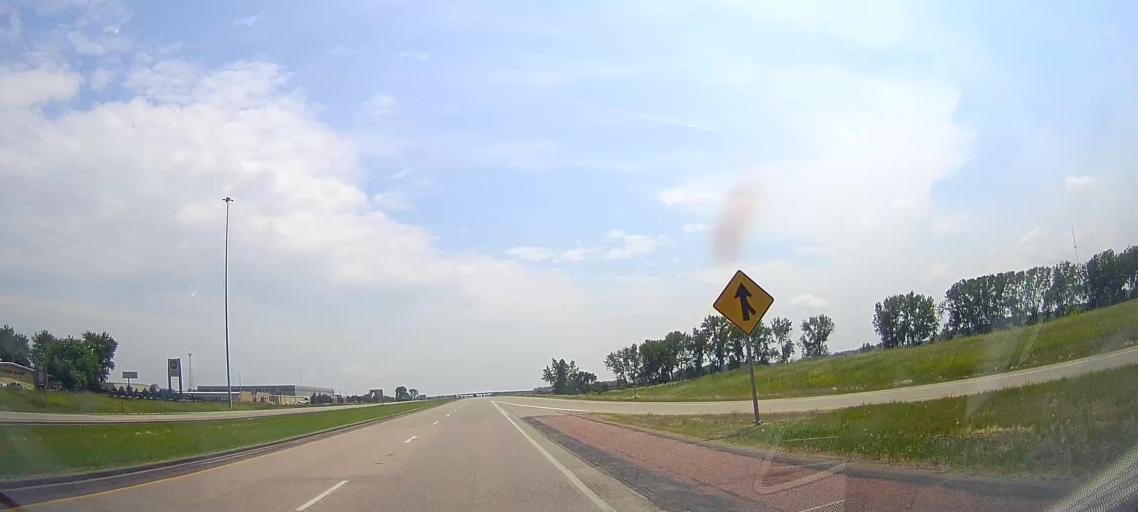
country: US
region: South Dakota
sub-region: Union County
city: Beresford
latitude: 43.0814
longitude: -96.7964
